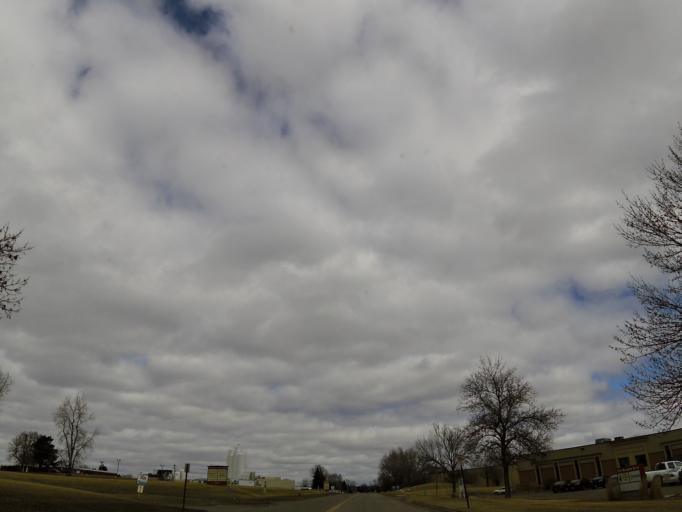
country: US
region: Minnesota
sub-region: Washington County
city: Woodbury
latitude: 44.9182
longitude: -92.9738
